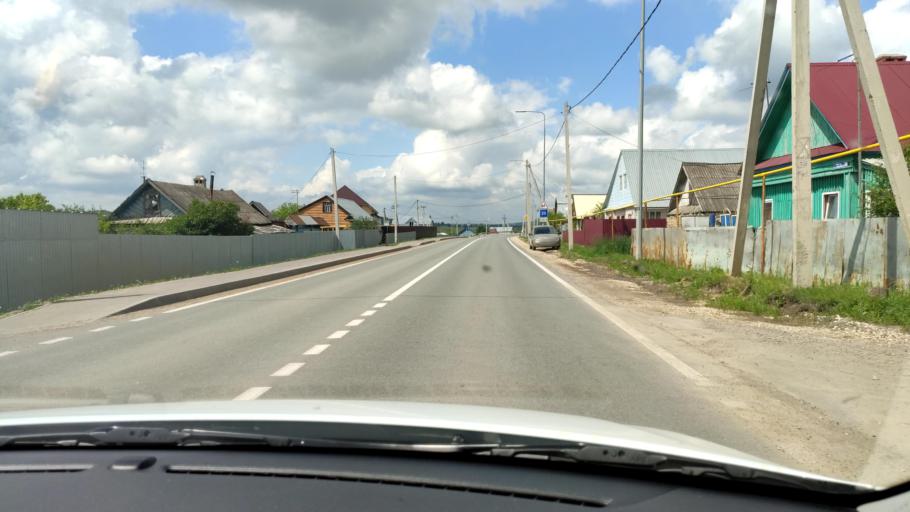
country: RU
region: Tatarstan
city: Vysokaya Gora
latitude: 55.9968
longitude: 49.3007
